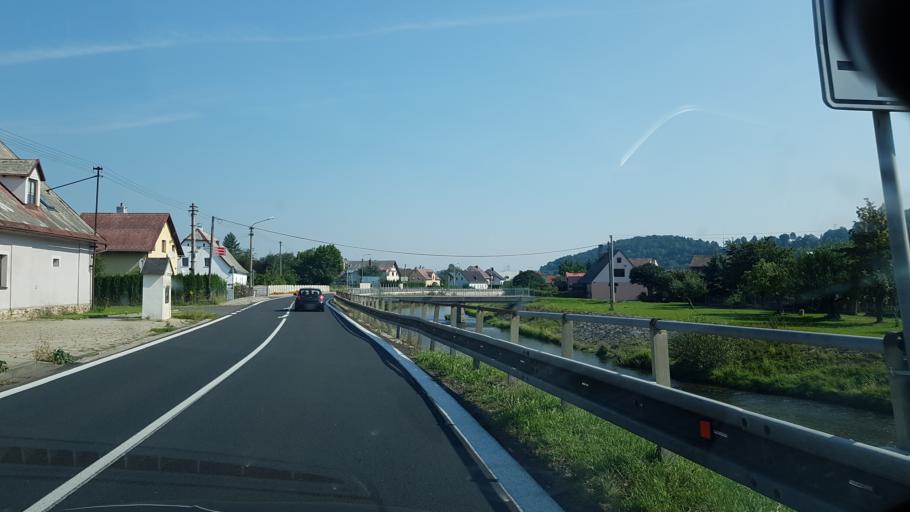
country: CZ
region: Olomoucky
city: Ceska Ves
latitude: 50.2602
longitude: 17.2347
